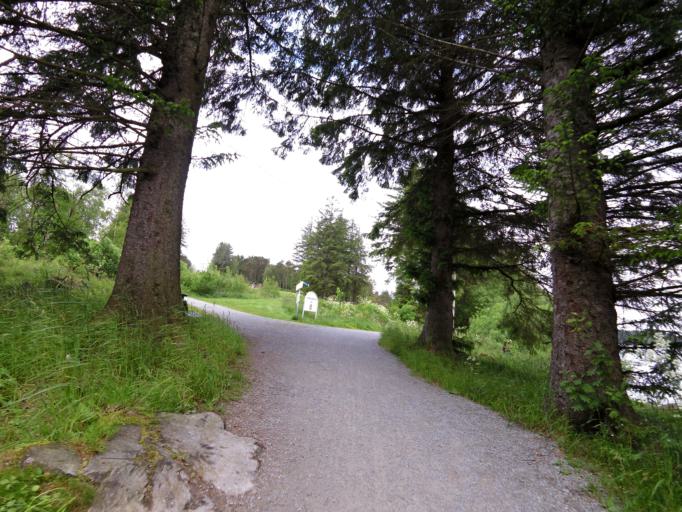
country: NO
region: Rogaland
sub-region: Randaberg
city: Randaberg
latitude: 58.9596
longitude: 5.6695
